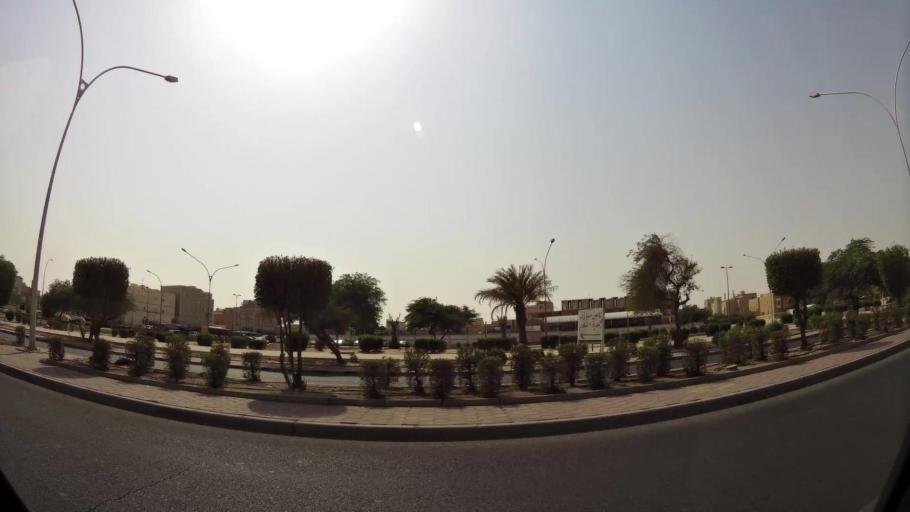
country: KW
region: Muhafazat al Jahra'
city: Al Jahra'
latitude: 29.3363
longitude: 47.6965
